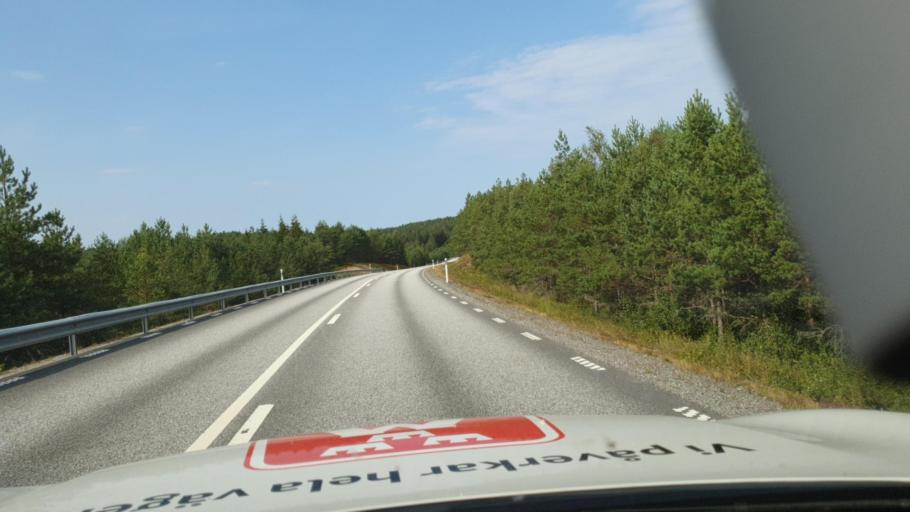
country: SE
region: Vaestra Goetaland
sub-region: Dals-Ed Kommun
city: Ed
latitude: 58.8413
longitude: 11.6519
